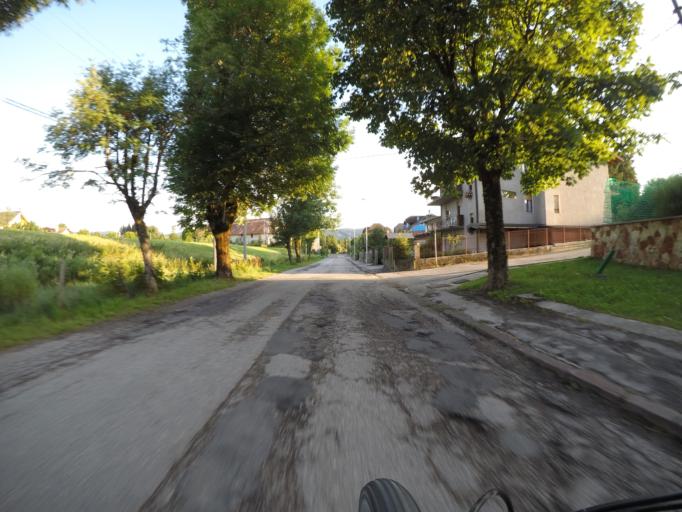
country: IT
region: Veneto
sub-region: Provincia di Vicenza
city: Asiago
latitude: 45.8812
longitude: 11.5191
